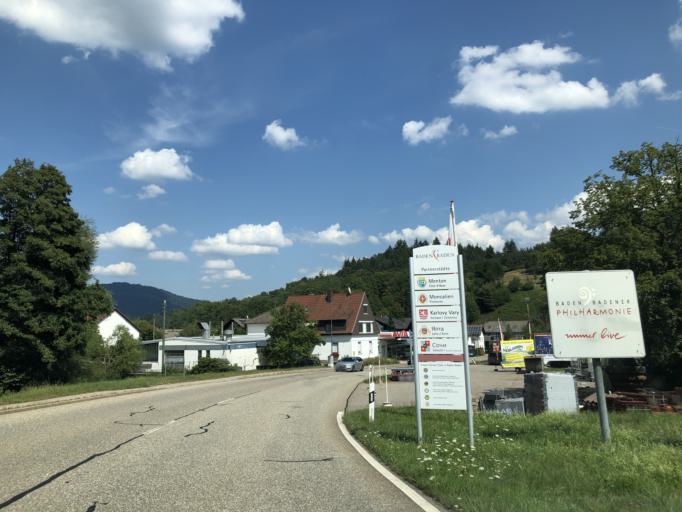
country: DE
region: Baden-Wuerttemberg
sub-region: Karlsruhe Region
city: Baden-Baden
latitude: 48.7242
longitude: 8.2450
